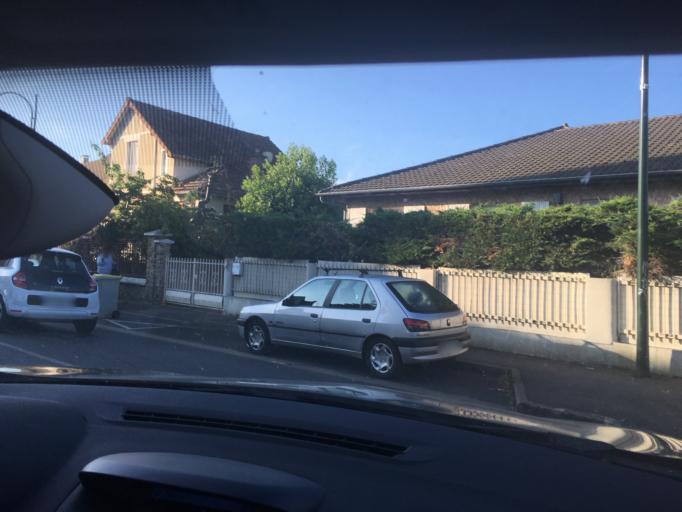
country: FR
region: Ile-de-France
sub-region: Departement de l'Essonne
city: Brunoy
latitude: 48.6928
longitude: 2.4912
